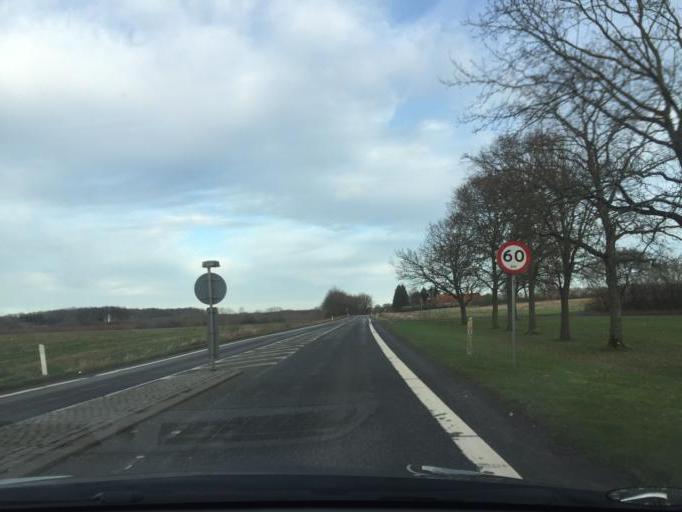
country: DK
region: South Denmark
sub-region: Faaborg-Midtfyn Kommune
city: Ringe
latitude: 55.2208
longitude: 10.4391
